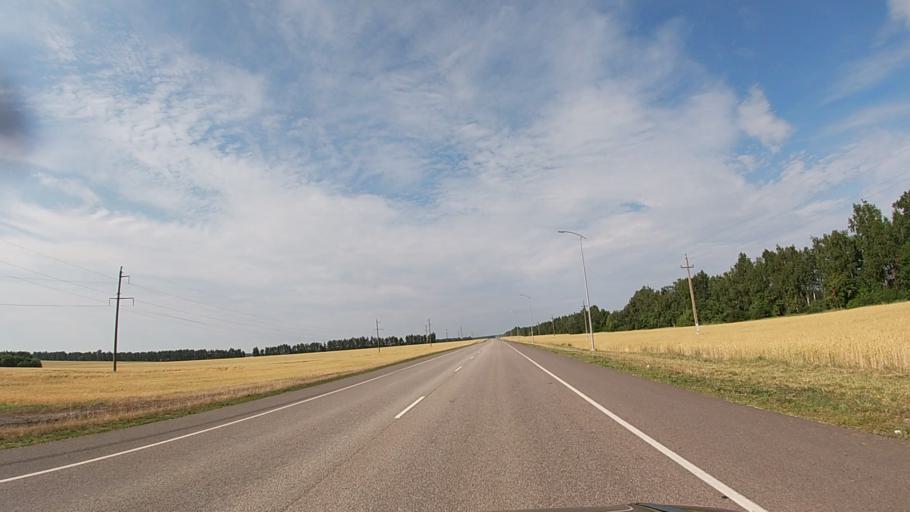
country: RU
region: Belgorod
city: Proletarskiy
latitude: 50.8270
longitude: 35.7612
